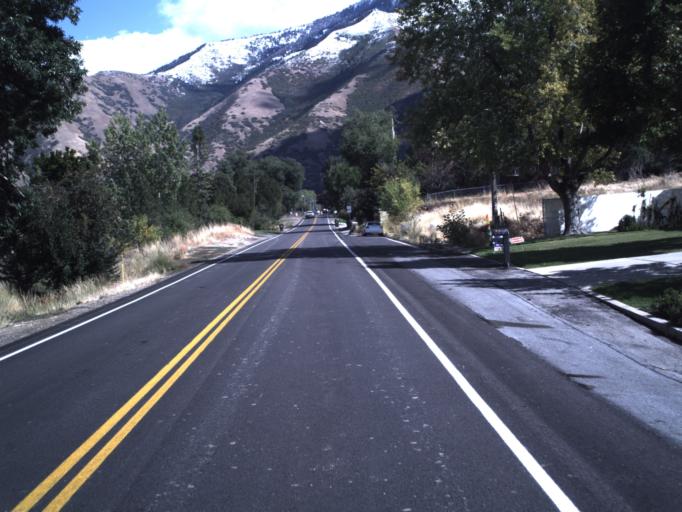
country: US
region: Utah
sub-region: Utah County
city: Mapleton
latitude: 40.1158
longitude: -111.5823
